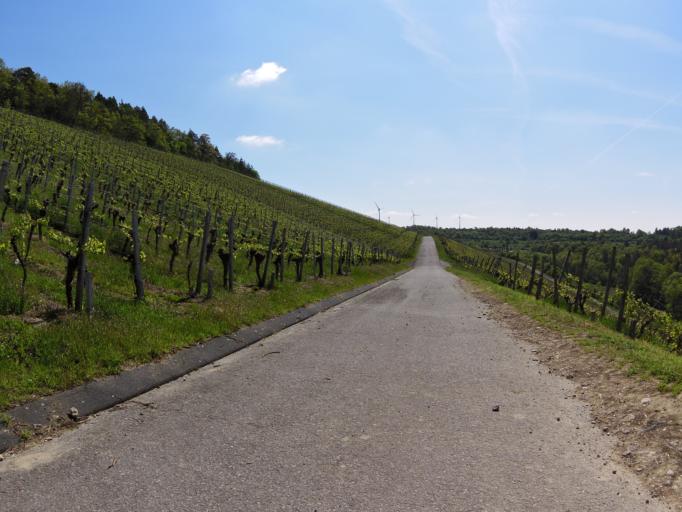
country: DE
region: Bavaria
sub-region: Regierungsbezirk Unterfranken
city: Eibelstadt
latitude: 49.7352
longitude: 10.0133
